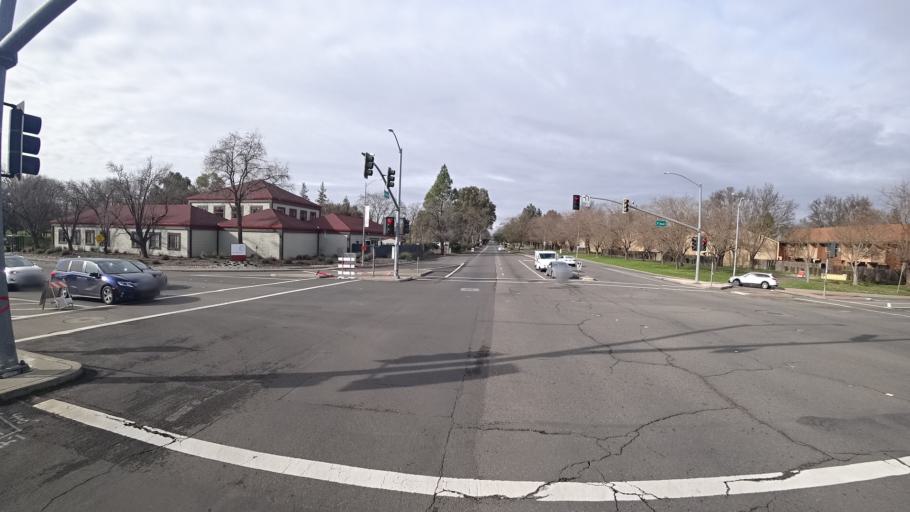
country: US
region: California
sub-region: Yolo County
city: Davis
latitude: 38.5606
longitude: -121.7448
